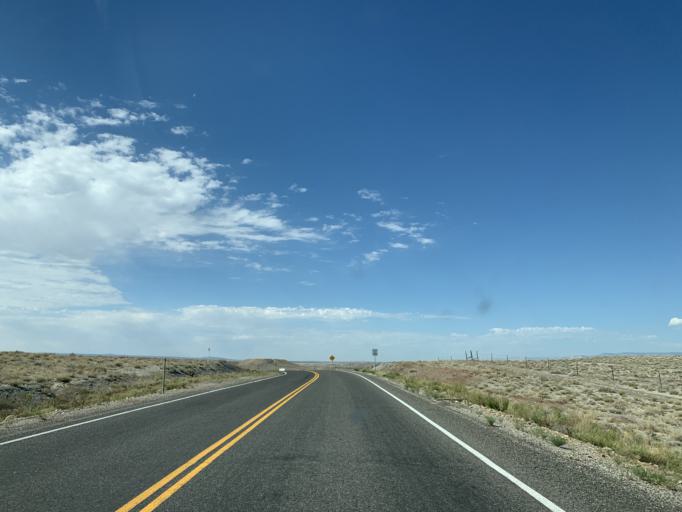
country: US
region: Utah
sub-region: Carbon County
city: Wellington
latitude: 39.5578
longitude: -110.6657
